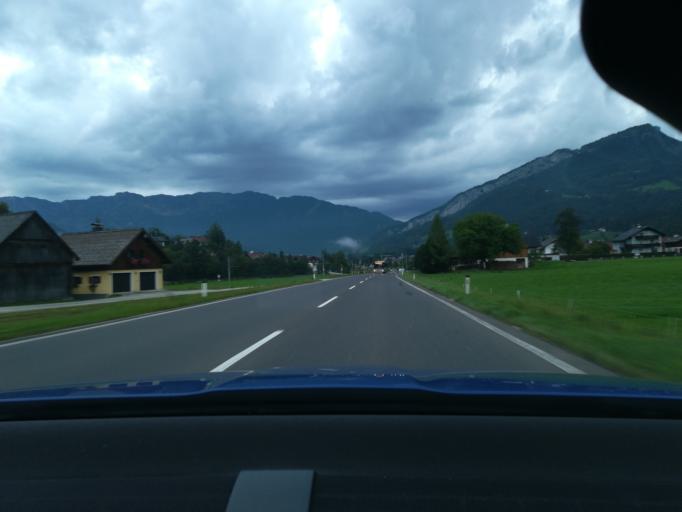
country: AT
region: Upper Austria
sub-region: Politischer Bezirk Gmunden
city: Bad Goisern
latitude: 47.6261
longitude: 13.6298
